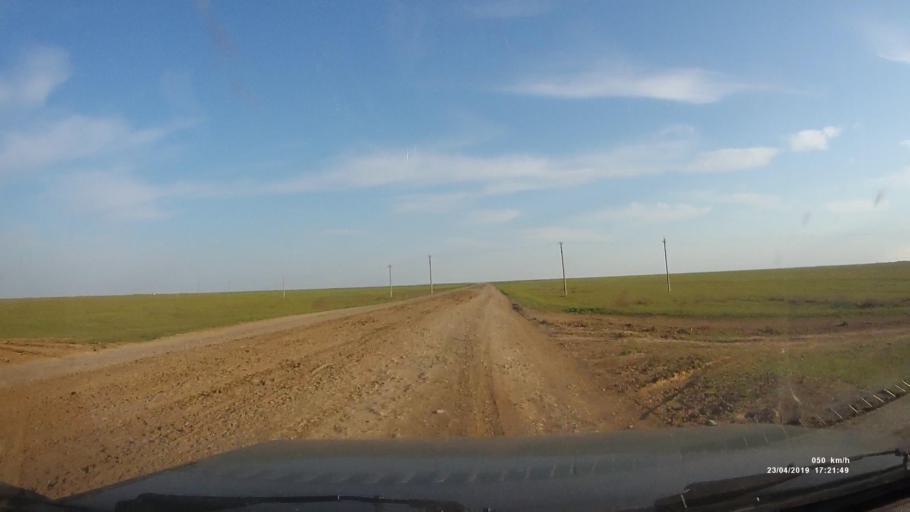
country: RU
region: Kalmykiya
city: Priyutnoye
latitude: 46.1731
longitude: 43.5058
